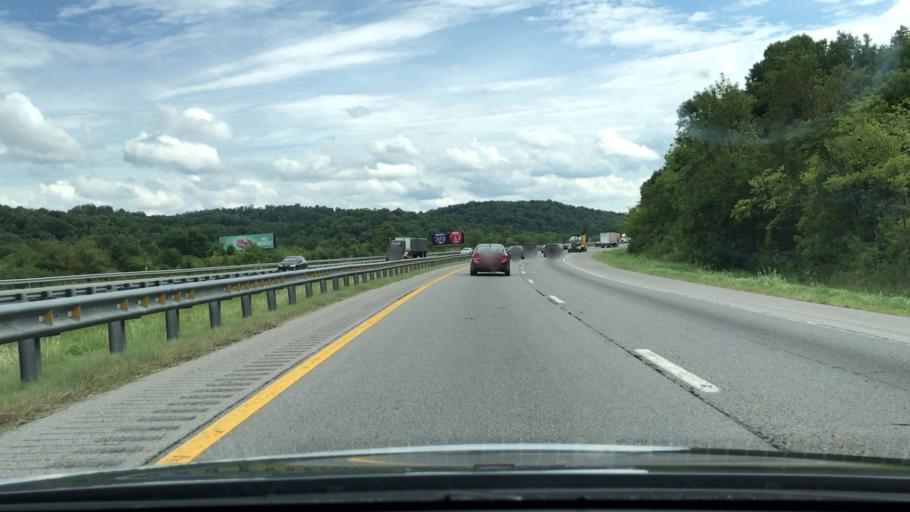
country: US
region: Tennessee
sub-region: Sumner County
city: White House
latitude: 36.4899
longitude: -86.6452
